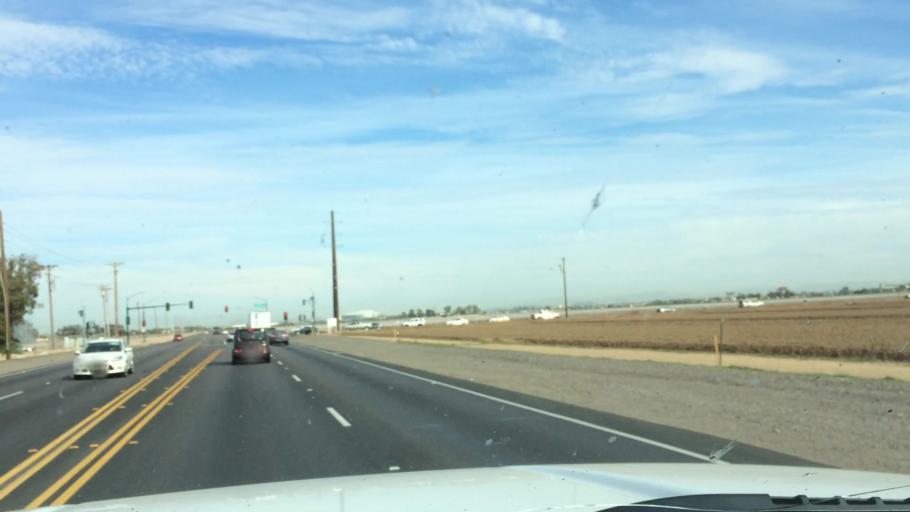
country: US
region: Arizona
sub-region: Maricopa County
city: Tolleson
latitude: 33.4778
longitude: -112.2725
